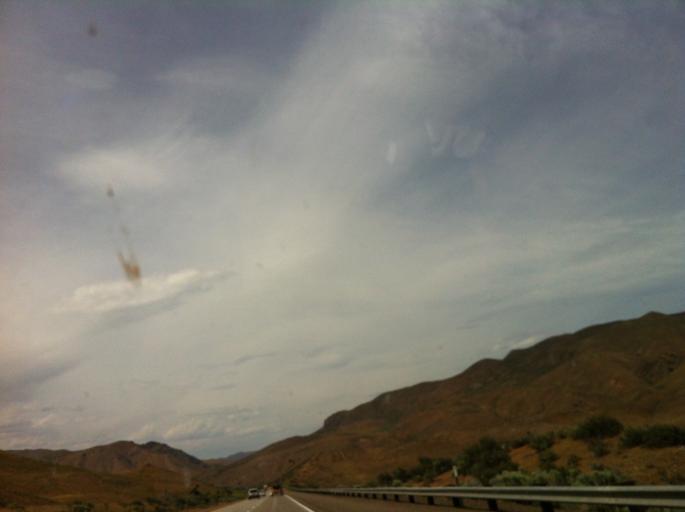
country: US
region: Idaho
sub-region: Washington County
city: Weiser
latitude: 44.3594
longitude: -117.2920
